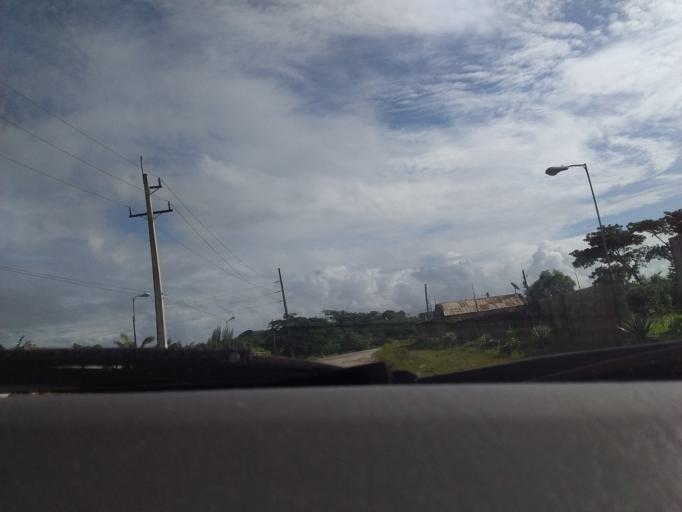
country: DO
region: Santo Domingo
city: Guerra
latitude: 18.5593
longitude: -69.7894
